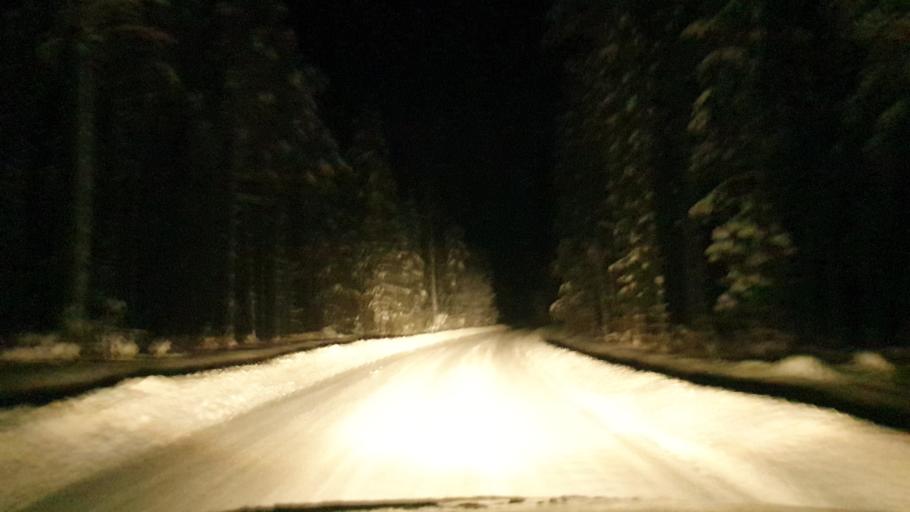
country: EE
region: Vorumaa
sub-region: Antsla vald
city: Vana-Antsla
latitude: 57.9688
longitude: 26.7258
